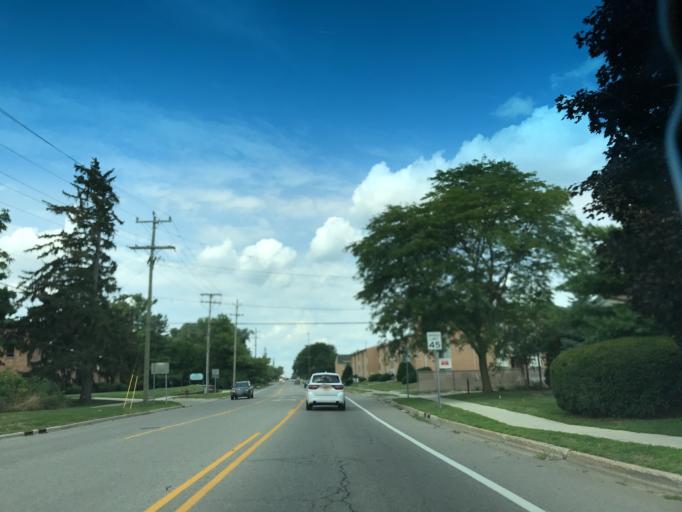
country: US
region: Michigan
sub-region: Washtenaw County
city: Ypsilanti
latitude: 42.2454
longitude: -83.6611
